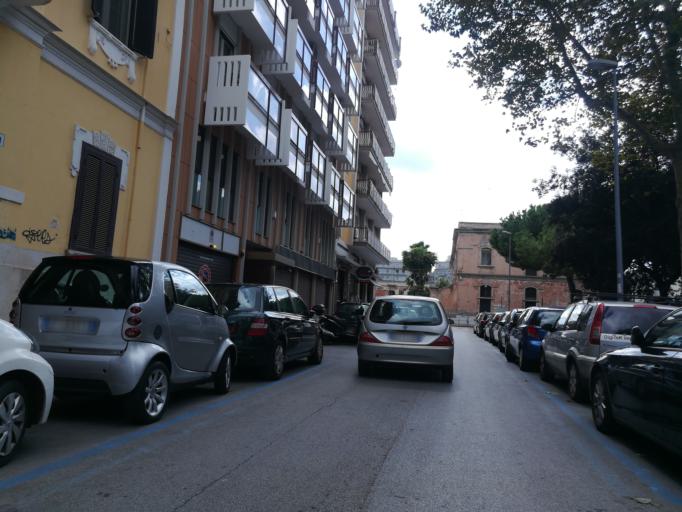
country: IT
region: Apulia
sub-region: Provincia di Bari
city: Bari
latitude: 41.1197
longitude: 16.8762
